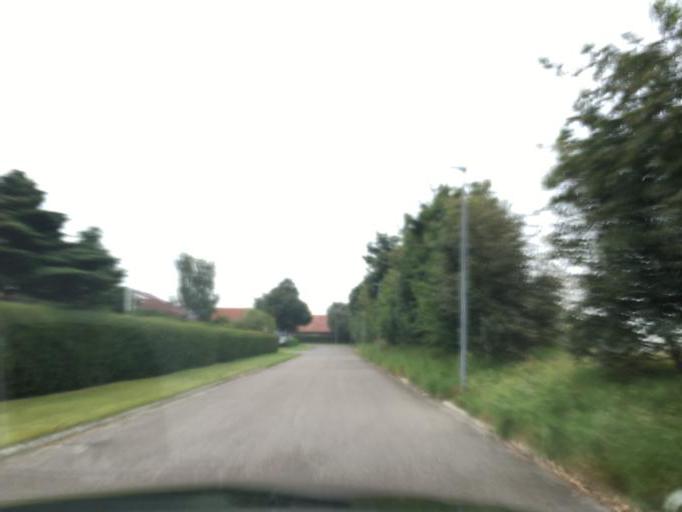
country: DK
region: South Denmark
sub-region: Kolding Kommune
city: Kolding
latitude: 55.5659
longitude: 9.4779
